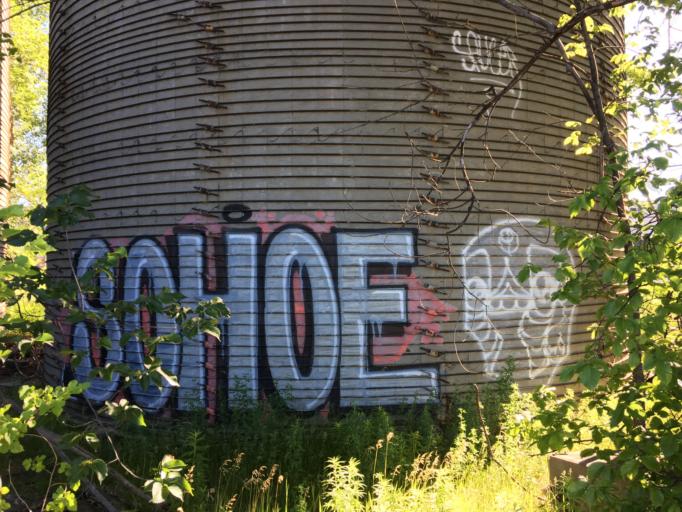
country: US
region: Michigan
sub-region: Wayne County
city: Dearborn
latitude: 42.3433
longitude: -83.1266
